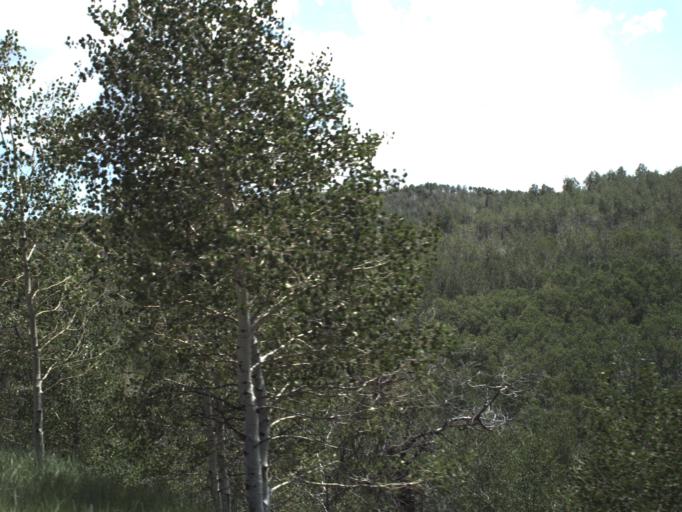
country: US
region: Utah
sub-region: Weber County
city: Wolf Creek
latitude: 41.4165
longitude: -111.5781
